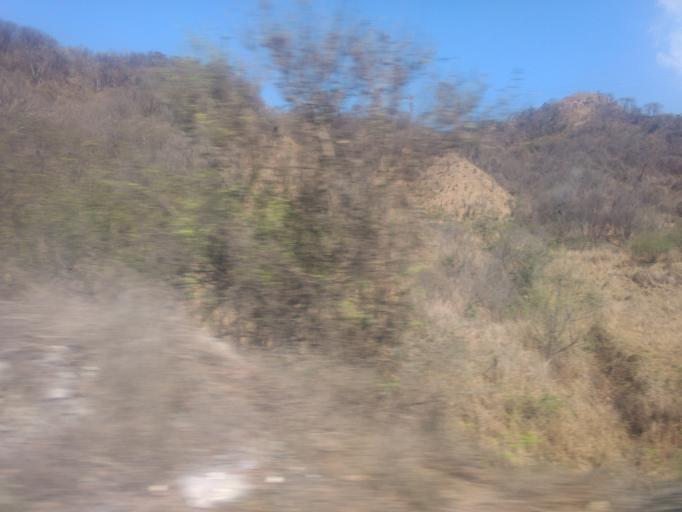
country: MX
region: Colima
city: El Colomo
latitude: 19.0535
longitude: -104.2687
